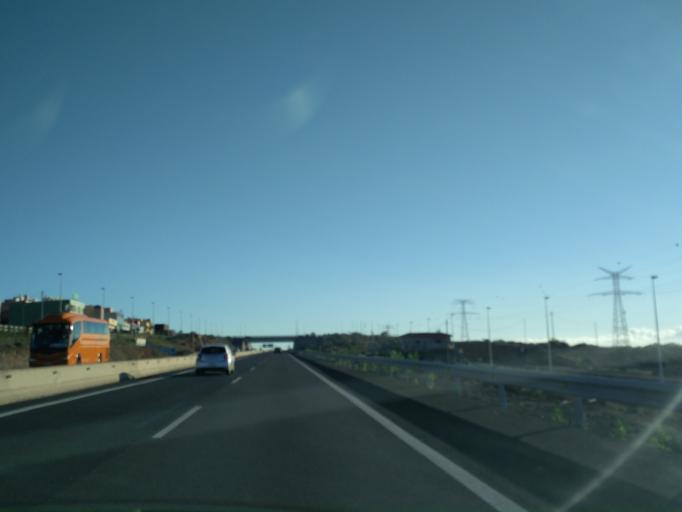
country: ES
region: Canary Islands
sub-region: Provincia de Santa Cruz de Tenerife
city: San Isidro
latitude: 28.0689
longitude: -16.5601
